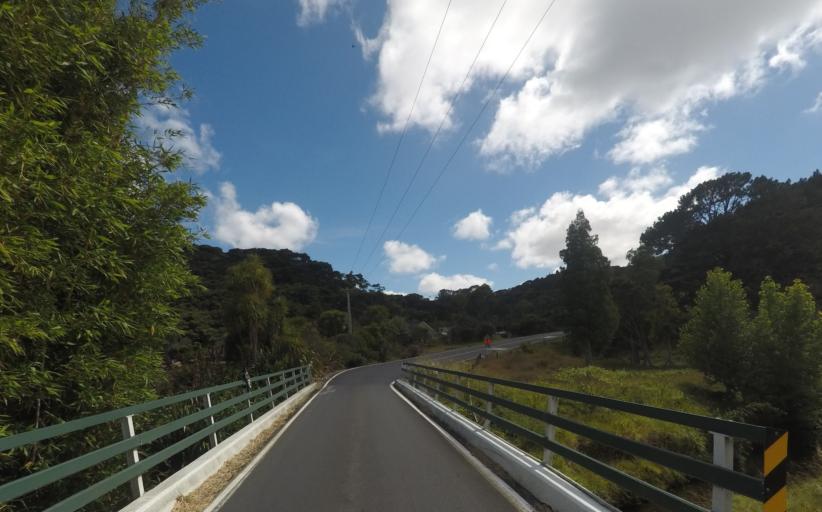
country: NZ
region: Auckland
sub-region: Auckland
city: Muriwai Beach
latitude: -36.8668
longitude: 174.5052
